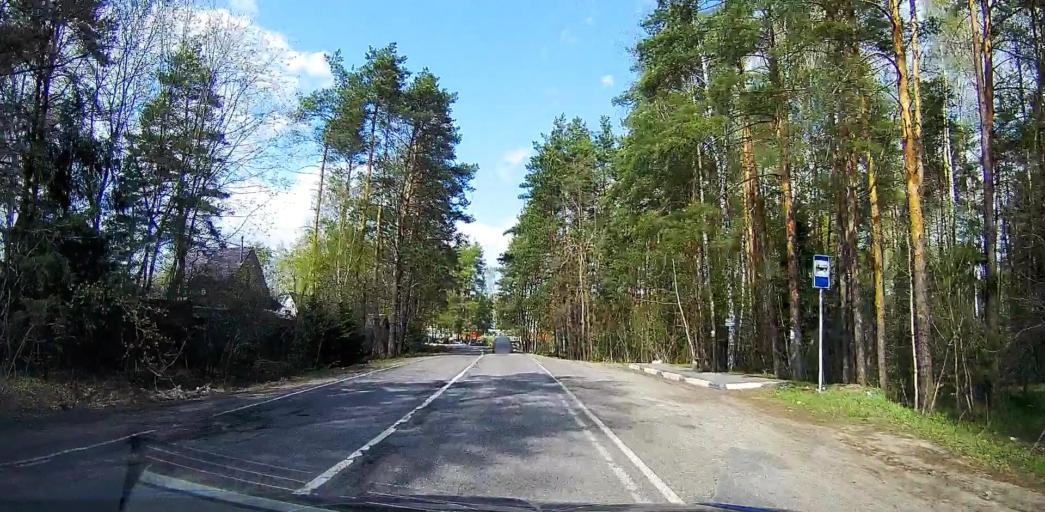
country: RU
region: Moskovskaya
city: Davydovo
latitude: 55.5707
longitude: 38.8232
